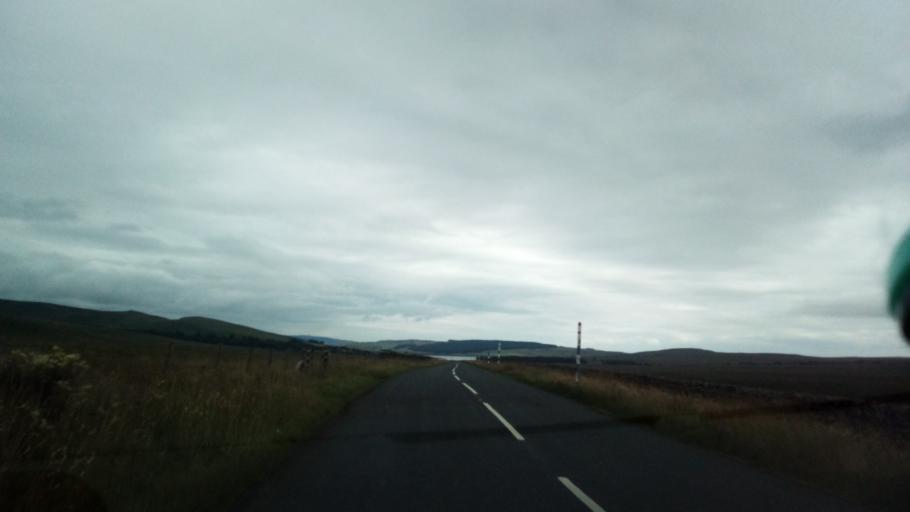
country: GB
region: England
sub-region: County Durham
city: Holwick
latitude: 54.5862
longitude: -2.1935
